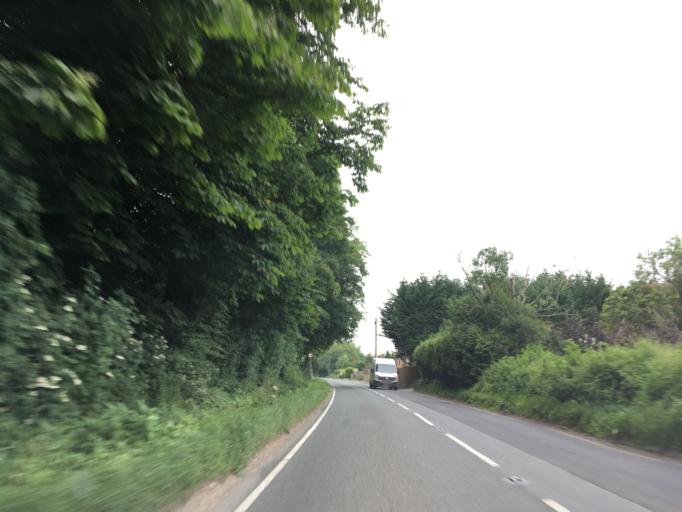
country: GB
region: England
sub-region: Gloucestershire
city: Stonehouse
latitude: 51.7681
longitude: -2.3550
